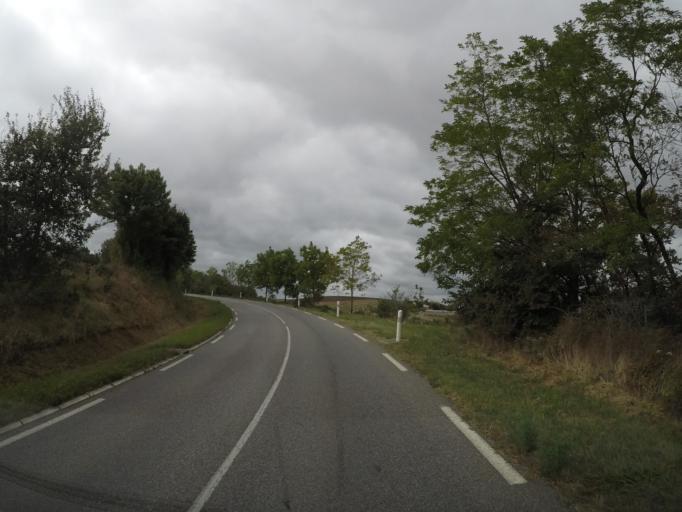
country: FR
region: Midi-Pyrenees
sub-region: Departement de la Haute-Garonne
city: Saint-Sulpice-sur-Leze
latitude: 43.3344
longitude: 1.3122
